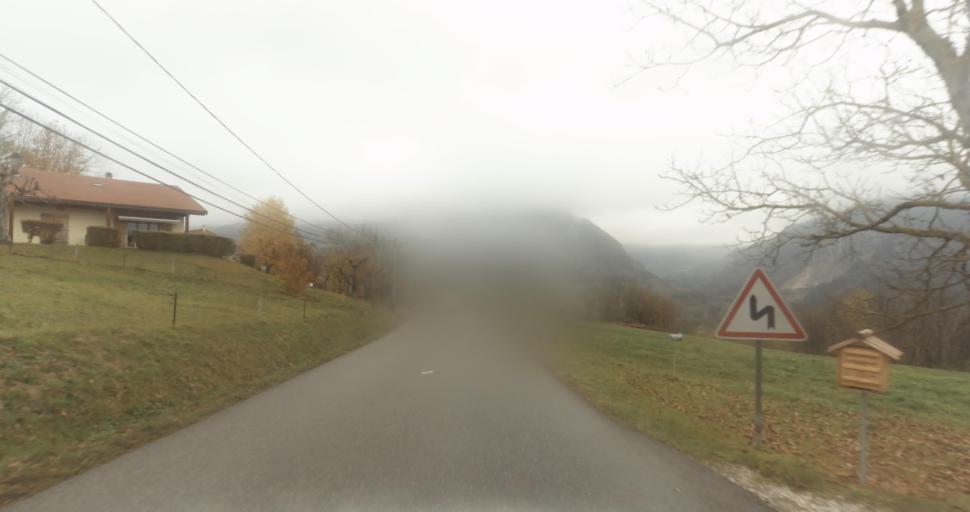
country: FR
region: Rhone-Alpes
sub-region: Departement de la Haute-Savoie
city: Thorens-Glieres
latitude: 46.0028
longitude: 6.2457
